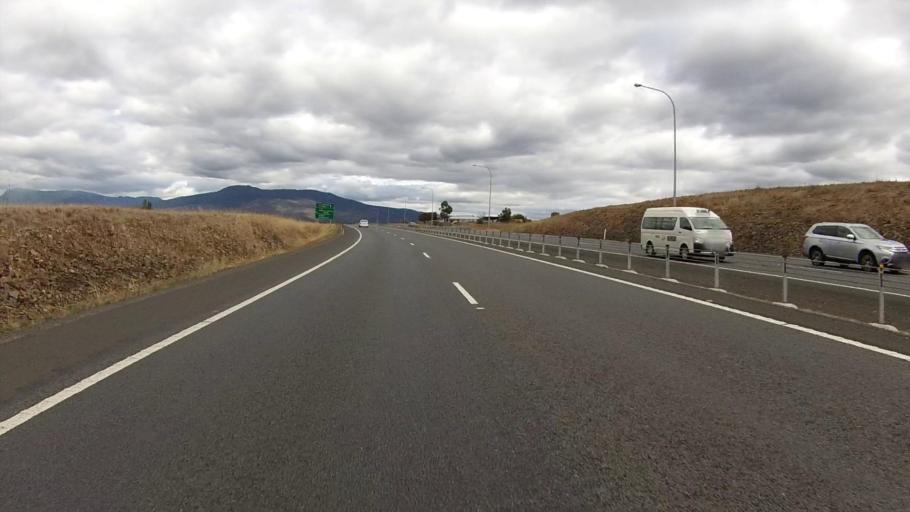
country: AU
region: Tasmania
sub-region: Brighton
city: Bridgewater
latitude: -42.7094
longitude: 147.2505
